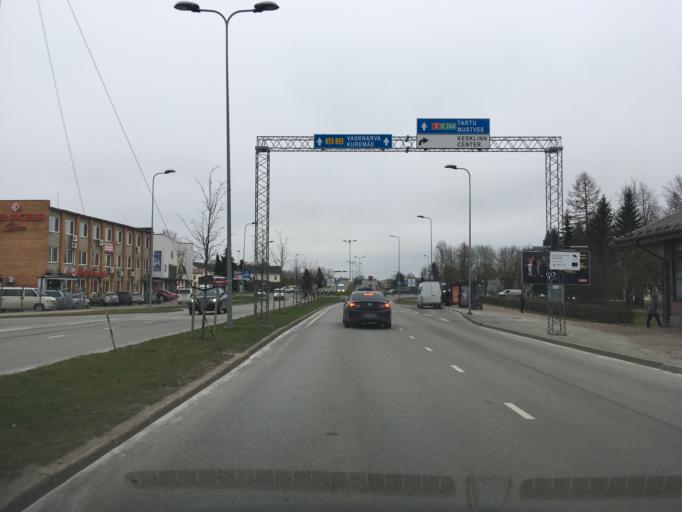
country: EE
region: Ida-Virumaa
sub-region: Johvi vald
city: Johvi
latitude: 59.3586
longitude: 27.4091
